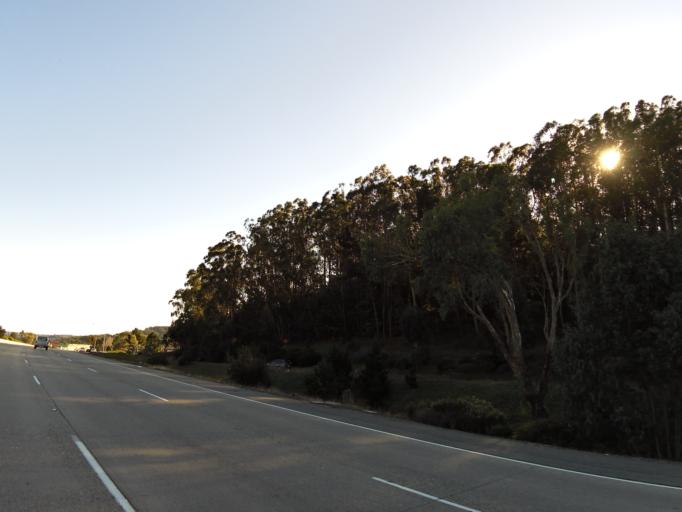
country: US
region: California
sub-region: San Mateo County
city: San Bruno
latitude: 37.6264
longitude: -122.4302
